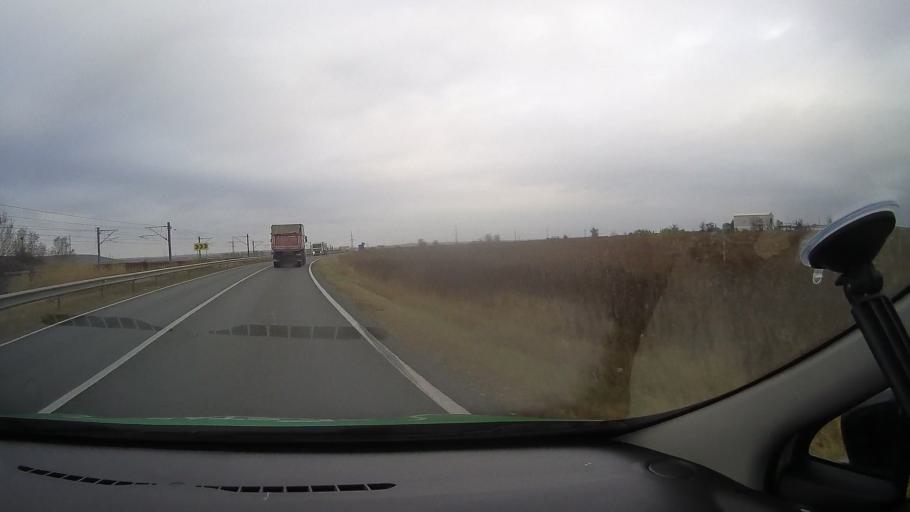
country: RO
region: Constanta
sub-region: Comuna Poarta Alba
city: Poarta Alba
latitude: 44.2296
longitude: 28.3789
